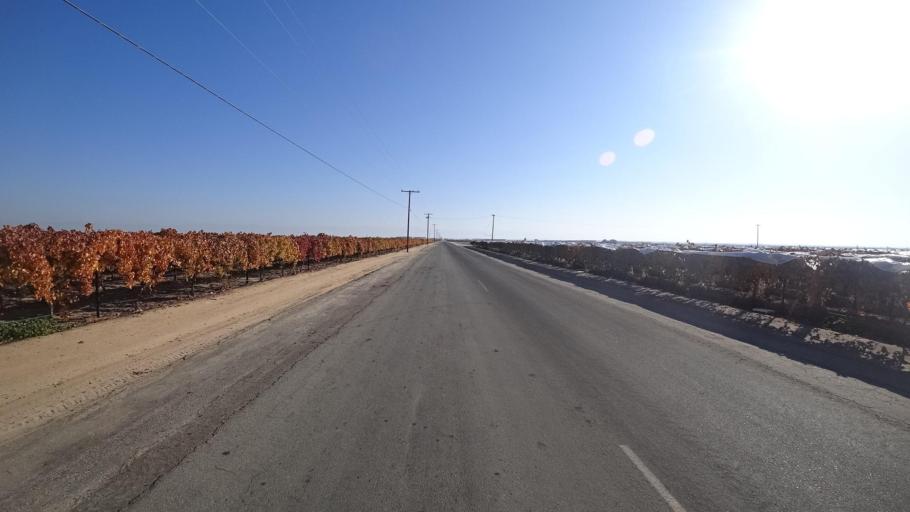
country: US
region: California
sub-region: Tulare County
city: Richgrove
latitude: 35.7470
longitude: -119.1577
